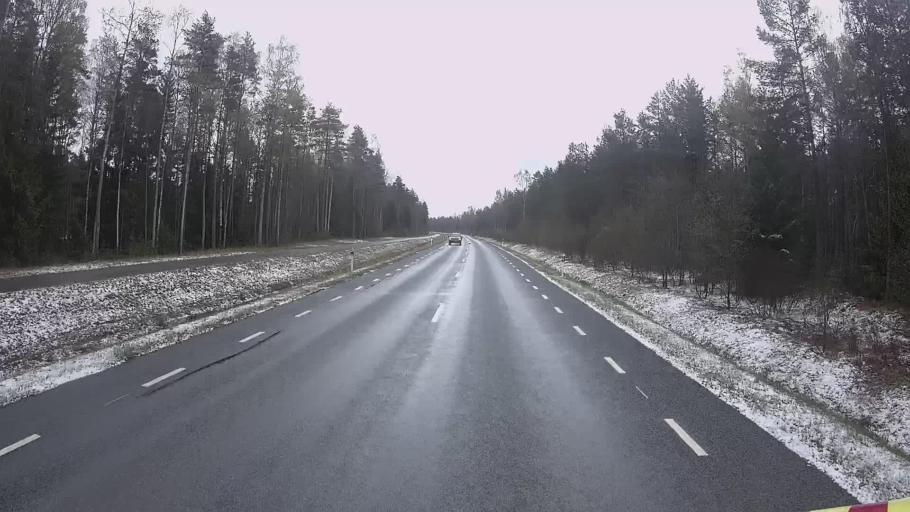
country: EE
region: Hiiumaa
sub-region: Kaerdla linn
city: Kardla
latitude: 59.0079
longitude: 22.6823
